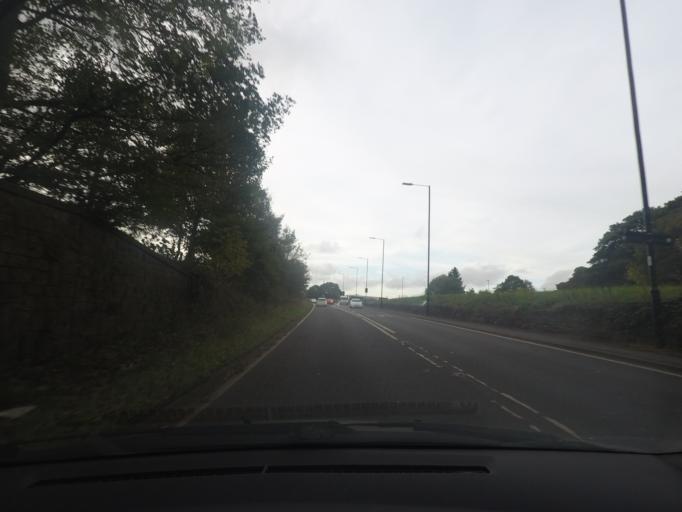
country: GB
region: England
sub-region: Sheffield
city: Chapletown
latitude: 53.4559
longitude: -1.4950
